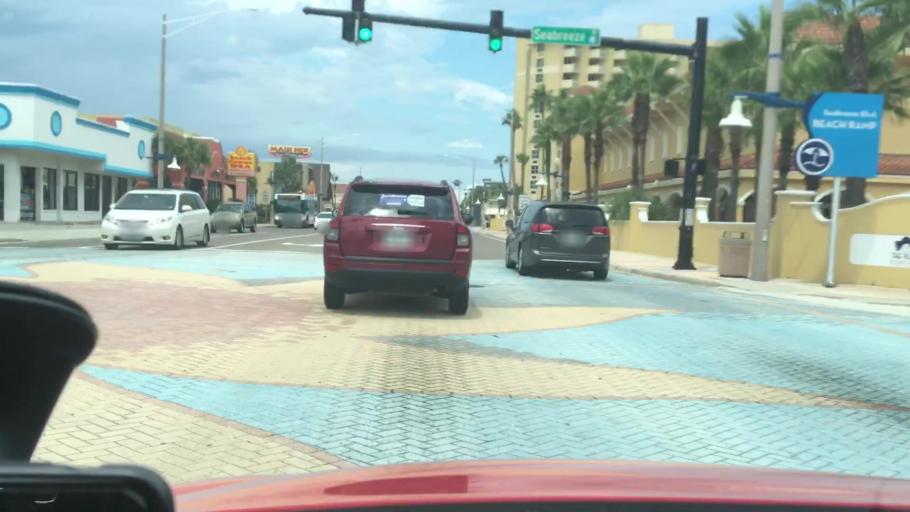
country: US
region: Florida
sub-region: Volusia County
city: Holly Hill
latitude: 29.2356
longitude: -81.0124
